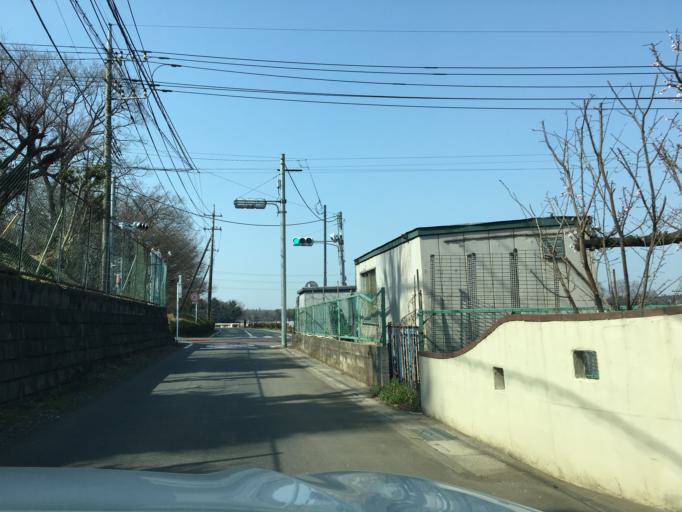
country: JP
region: Saitama
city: Kamifukuoka
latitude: 35.8669
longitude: 139.4968
